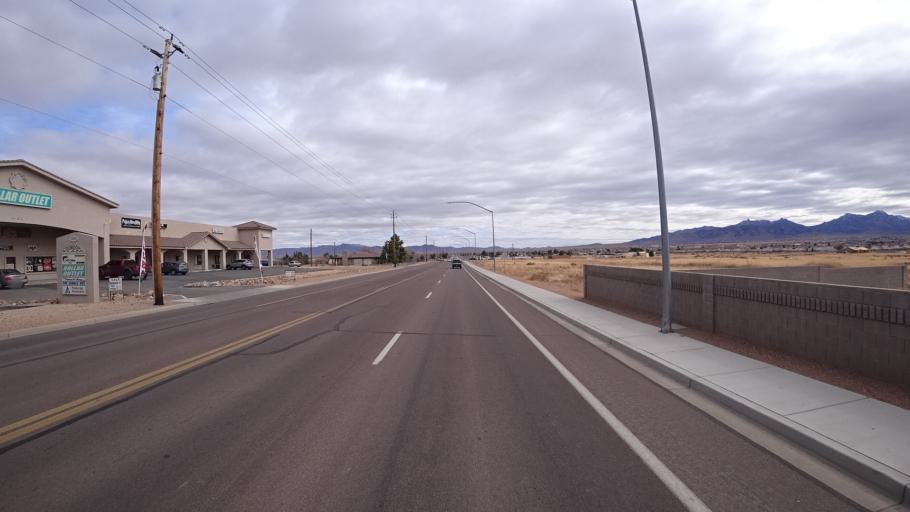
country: US
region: Arizona
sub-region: Mohave County
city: New Kingman-Butler
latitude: 35.2393
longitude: -114.0277
